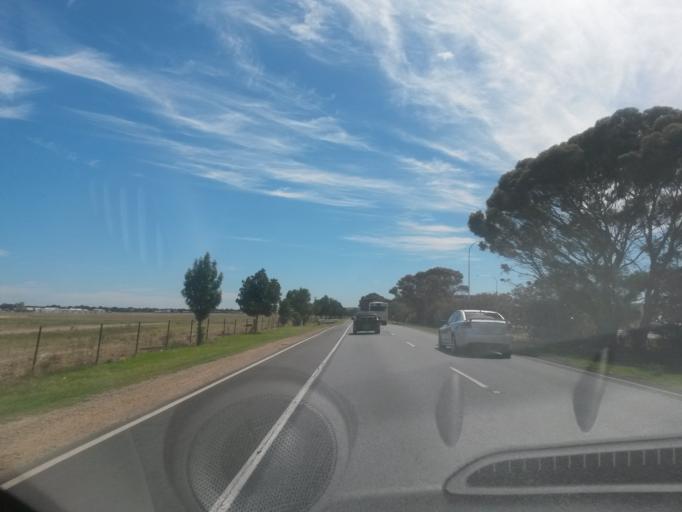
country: AU
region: South Australia
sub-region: Salisbury
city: Ingle Farm
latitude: -34.8052
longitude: 138.6348
